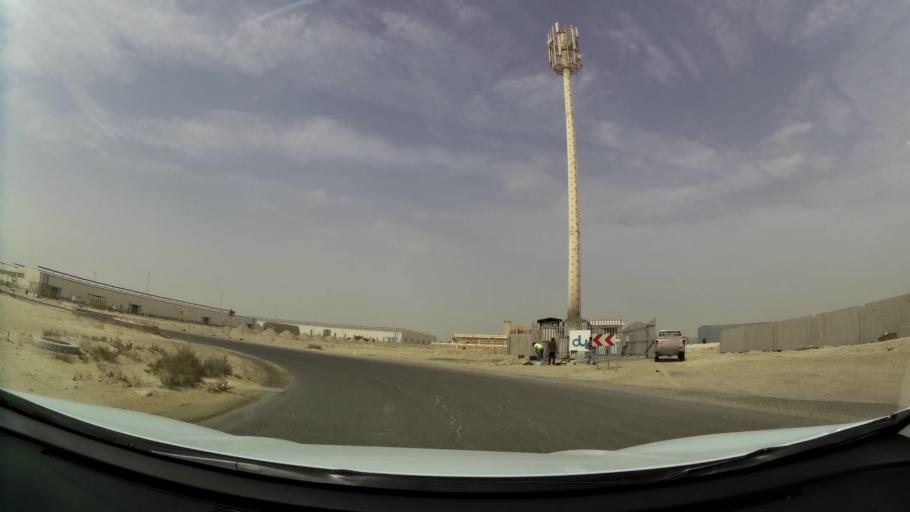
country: AE
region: Abu Dhabi
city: Abu Dhabi
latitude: 24.3290
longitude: 54.4844
